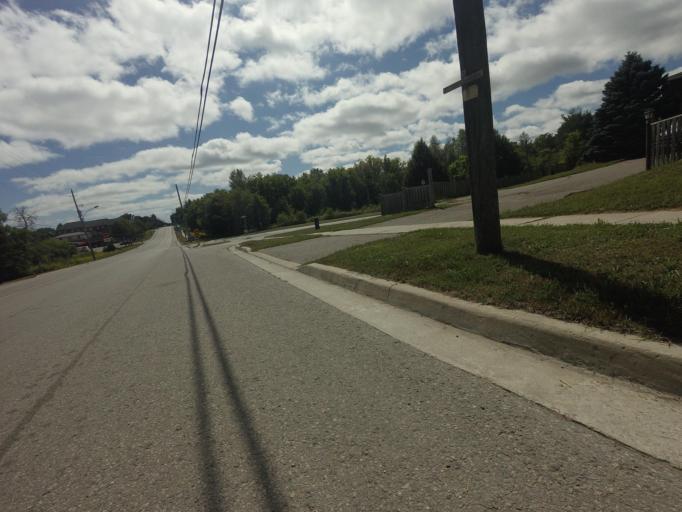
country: CA
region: Ontario
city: Uxbridge
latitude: 44.1197
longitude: -79.1251
